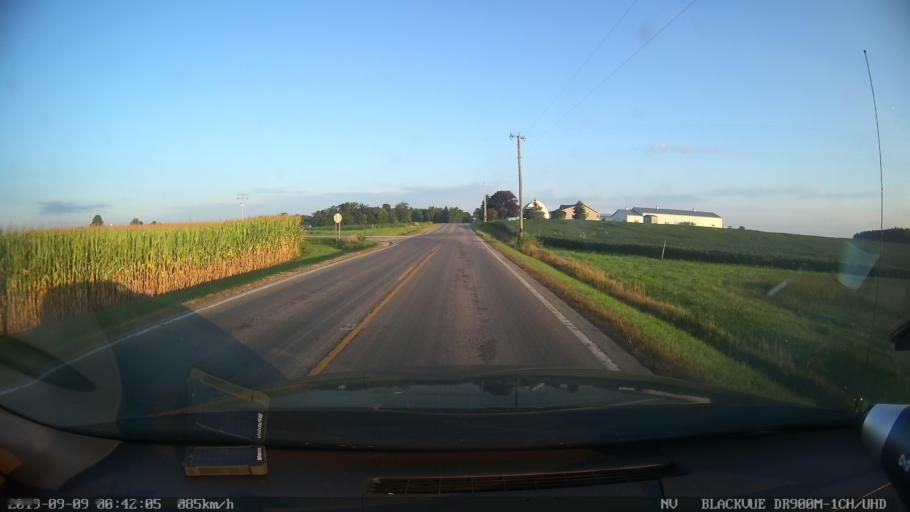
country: US
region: Ohio
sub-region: Crawford County
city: Bucyrus
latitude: 40.7613
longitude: -82.9158
